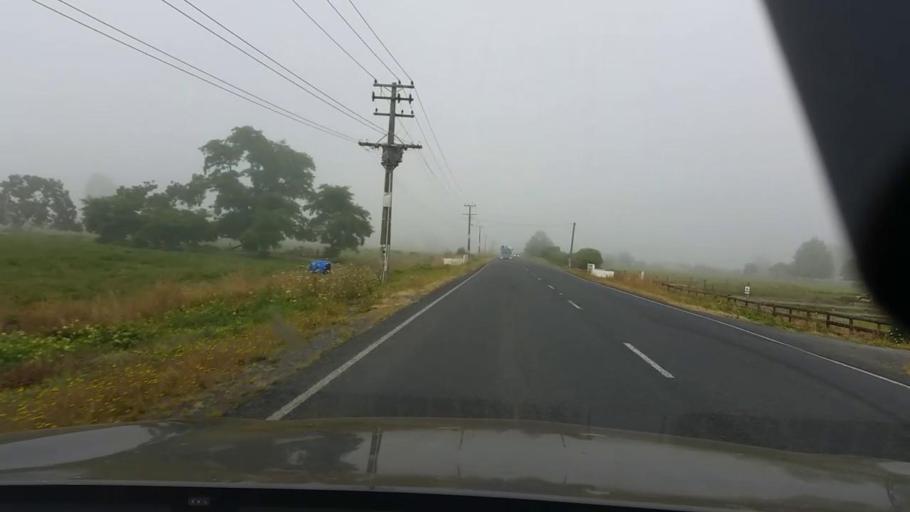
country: NZ
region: Waikato
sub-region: Hamilton City
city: Hamilton
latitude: -37.6330
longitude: 175.3074
